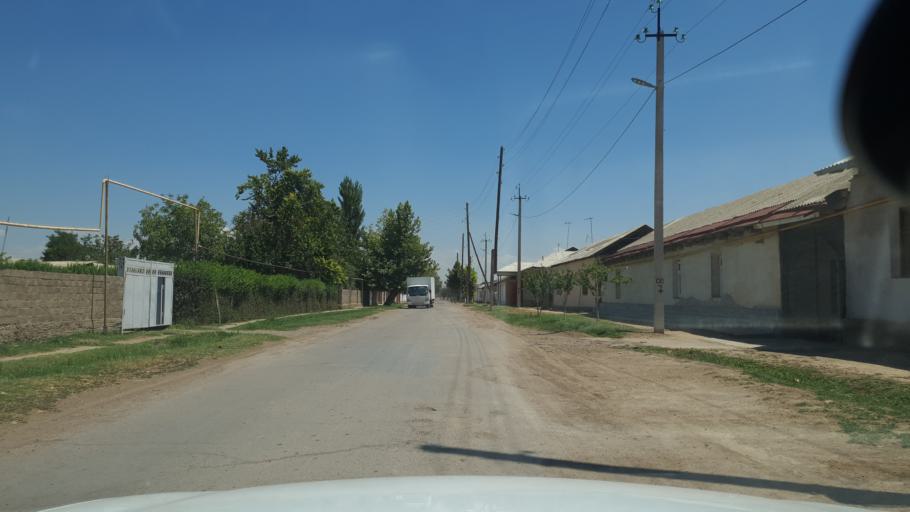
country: UZ
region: Toshkent
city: Piskent
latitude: 40.8268
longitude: 69.4068
